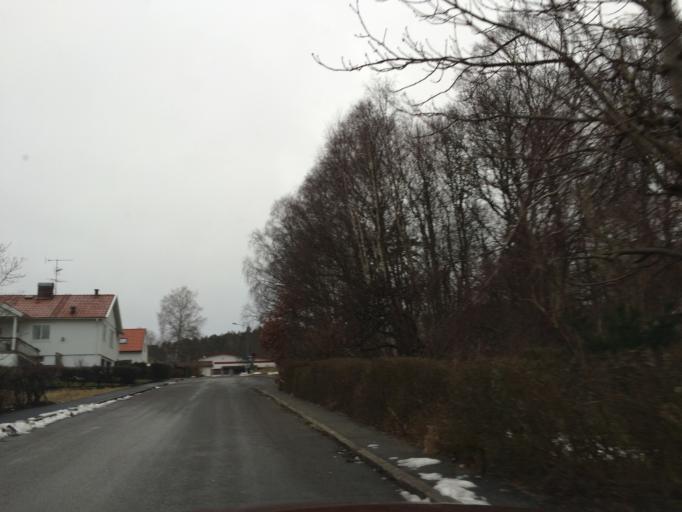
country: SE
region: Halland
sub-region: Kungsbacka Kommun
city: Kungsbacka
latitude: 57.4933
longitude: 12.0658
